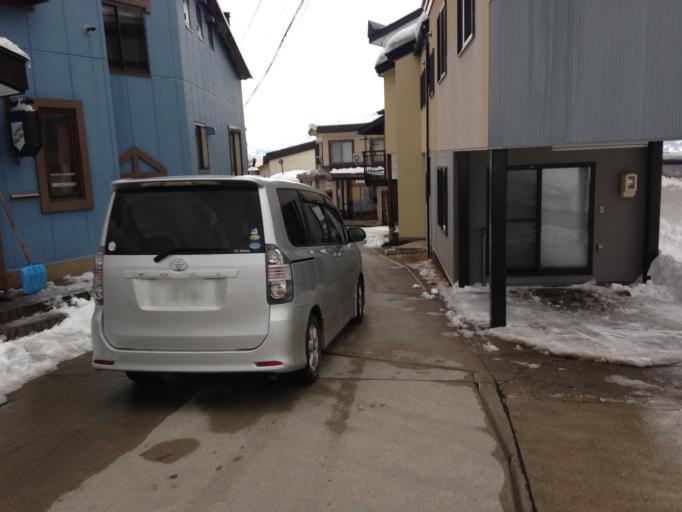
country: JP
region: Nagano
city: Iiyama
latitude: 36.9198
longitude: 138.4470
